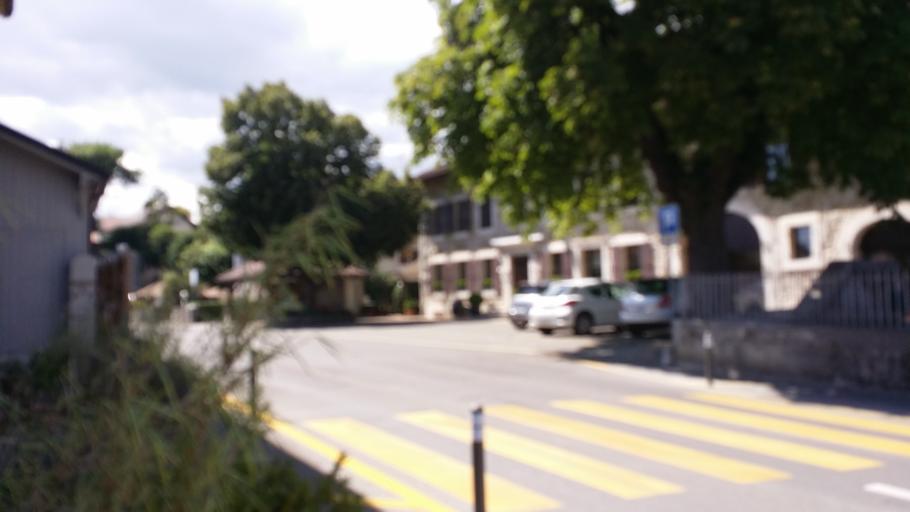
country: FR
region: Rhone-Alpes
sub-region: Departement de l'Ain
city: Divonne-les-Bains
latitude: 46.3813
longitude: 6.1523
